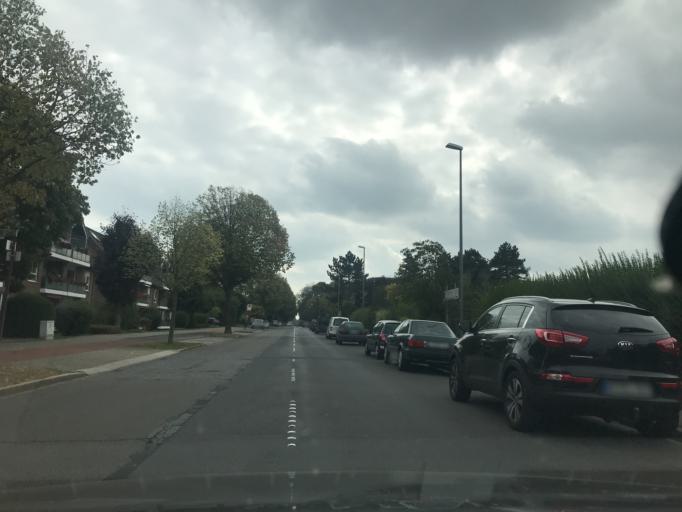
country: DE
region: North Rhine-Westphalia
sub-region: Regierungsbezirk Dusseldorf
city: Krefeld
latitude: 51.3665
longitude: 6.6375
